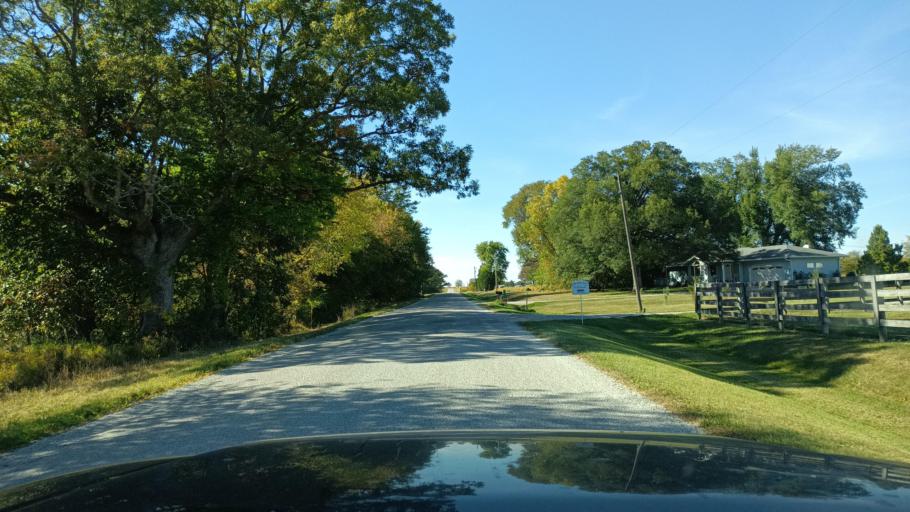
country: US
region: Illinois
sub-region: Logan County
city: Atlanta
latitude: 40.2390
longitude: -89.1761
